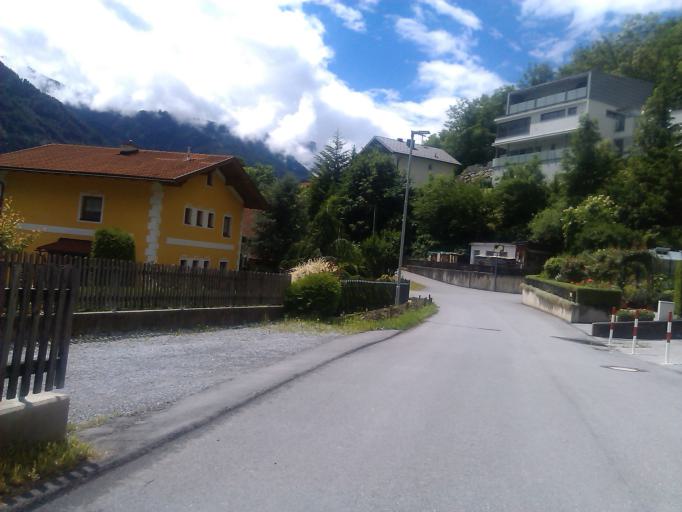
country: AT
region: Tyrol
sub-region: Politischer Bezirk Landeck
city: Prutz
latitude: 47.0853
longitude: 10.6602
